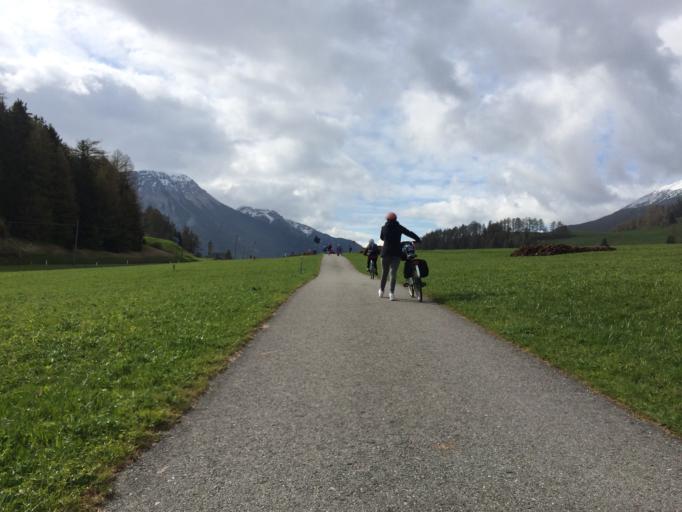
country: IT
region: Trentino-Alto Adige
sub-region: Bolzano
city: Curon Venosta
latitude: 46.8372
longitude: 10.5072
